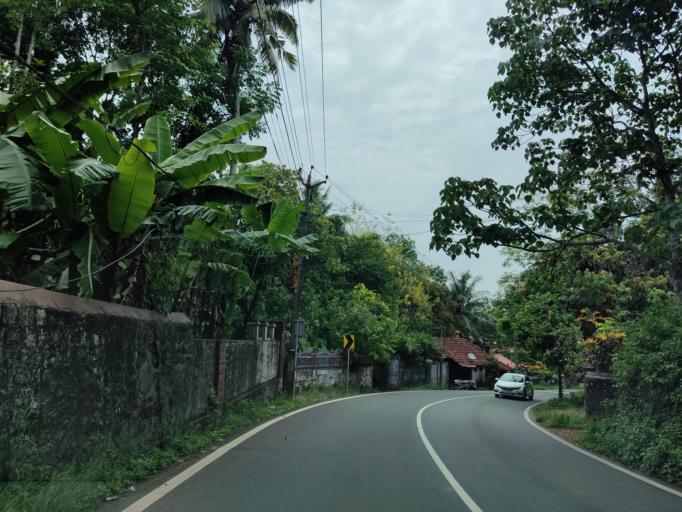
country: IN
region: Kerala
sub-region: Alappuzha
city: Chengannur
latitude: 9.2846
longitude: 76.6132
